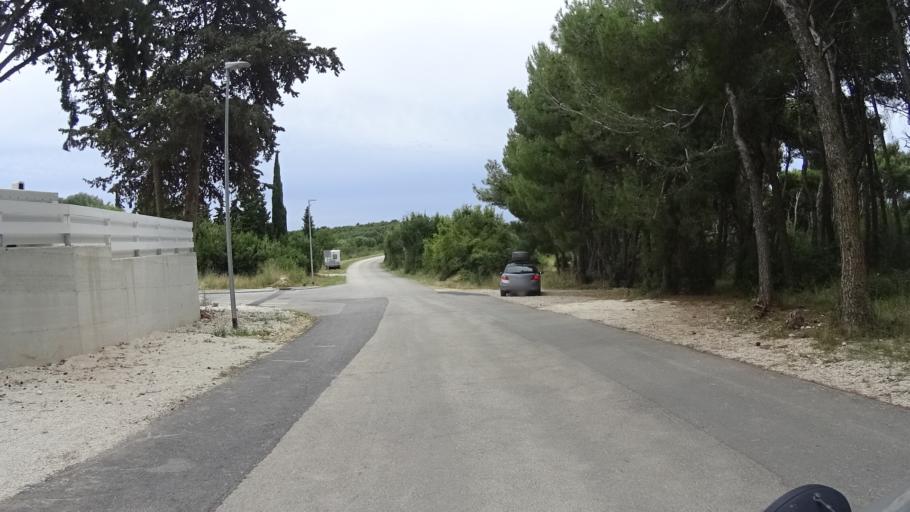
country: HR
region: Istarska
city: Medulin
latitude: 44.8019
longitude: 13.9062
